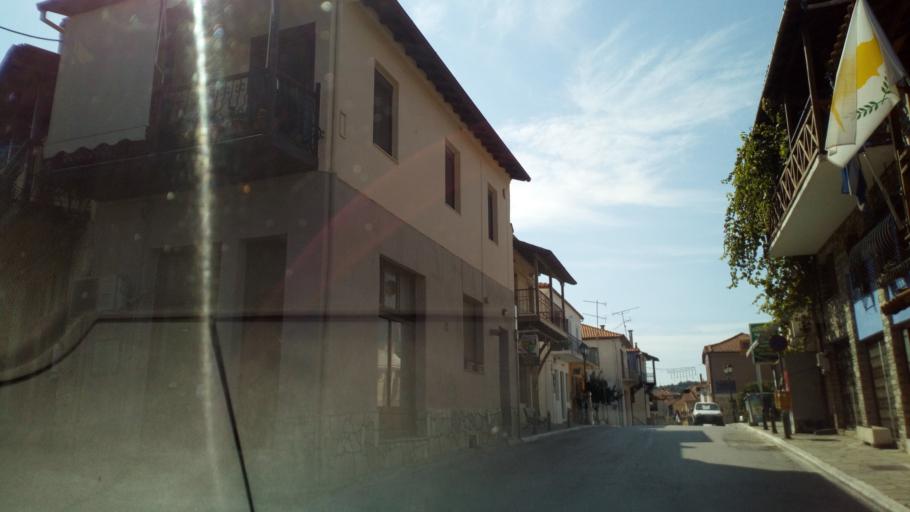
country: GR
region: Central Macedonia
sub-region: Nomos Chalkidikis
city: Arnaia
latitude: 40.4862
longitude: 23.5950
